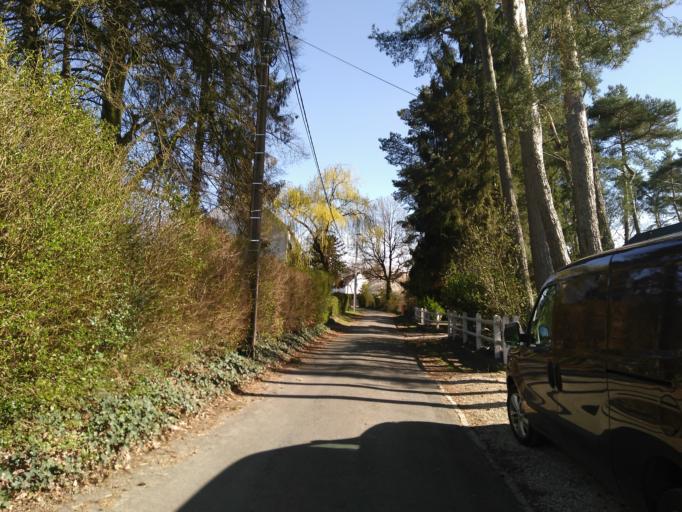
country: BE
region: Wallonia
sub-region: Province du Brabant Wallon
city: Chaumont-Gistoux
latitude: 50.6764
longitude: 4.6942
